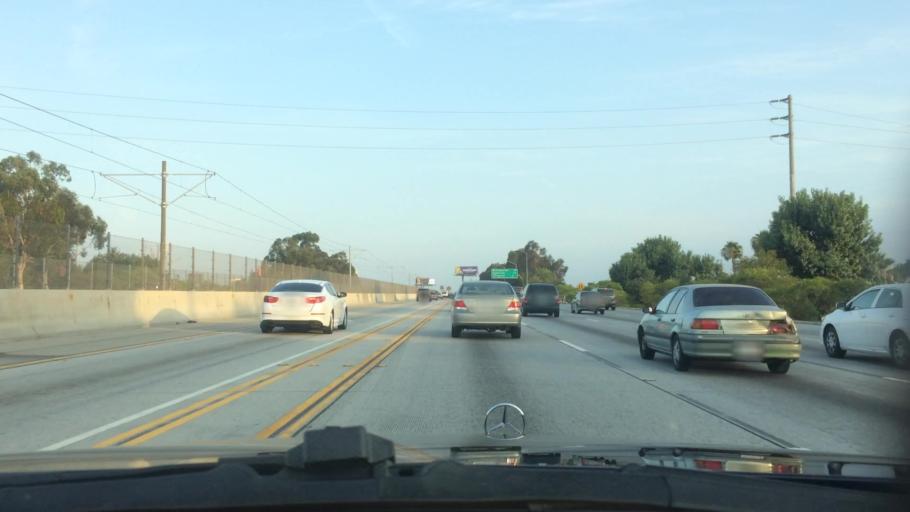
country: US
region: California
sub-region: Los Angeles County
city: Lynwood
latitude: 33.9273
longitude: -118.2151
